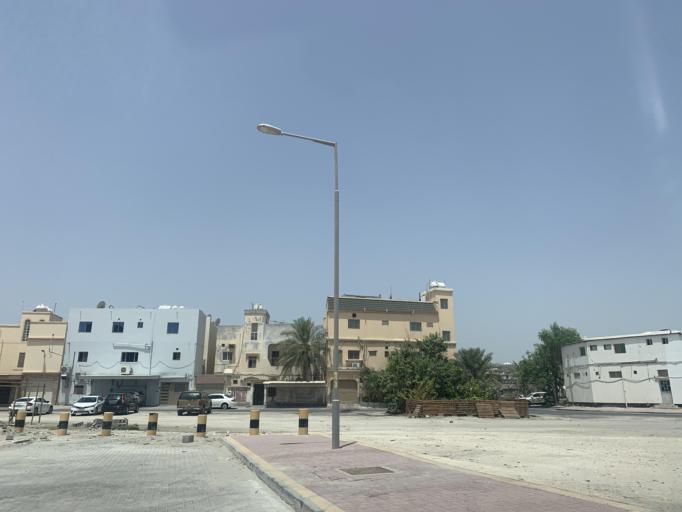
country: BH
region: Central Governorate
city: Madinat Hamad
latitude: 26.1436
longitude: 50.5009
